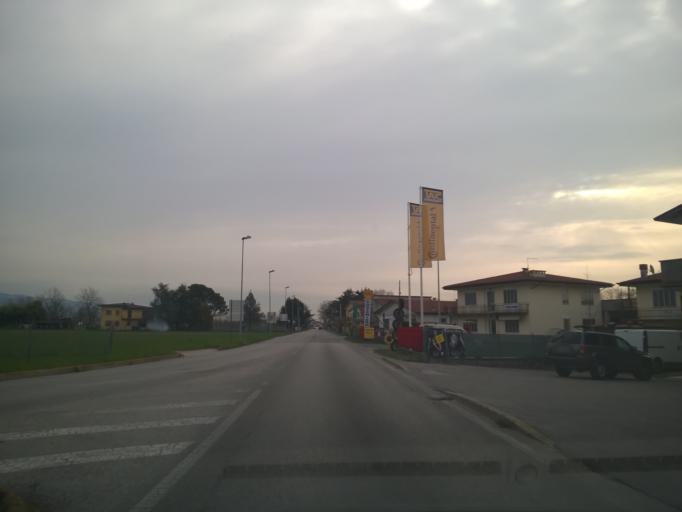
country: IT
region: Veneto
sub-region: Provincia di Vicenza
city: Marano Vicentino
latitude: 45.6937
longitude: 11.4484
